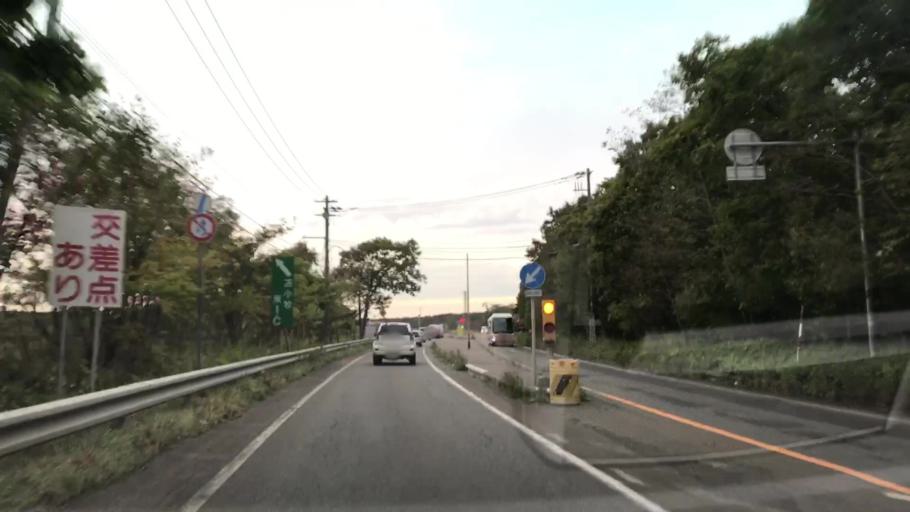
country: JP
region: Hokkaido
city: Tomakomai
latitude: 42.7066
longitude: 141.6619
